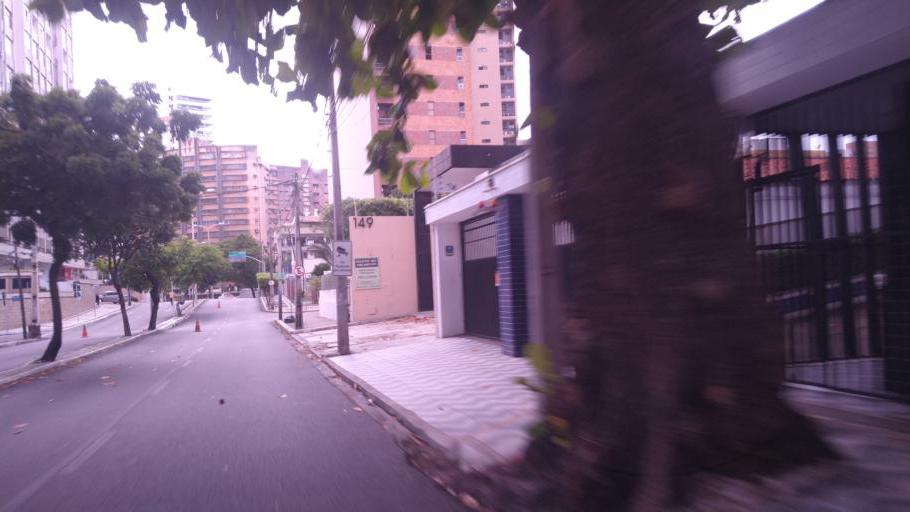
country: BR
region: Ceara
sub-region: Fortaleza
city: Fortaleza
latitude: -3.7304
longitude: -38.4911
